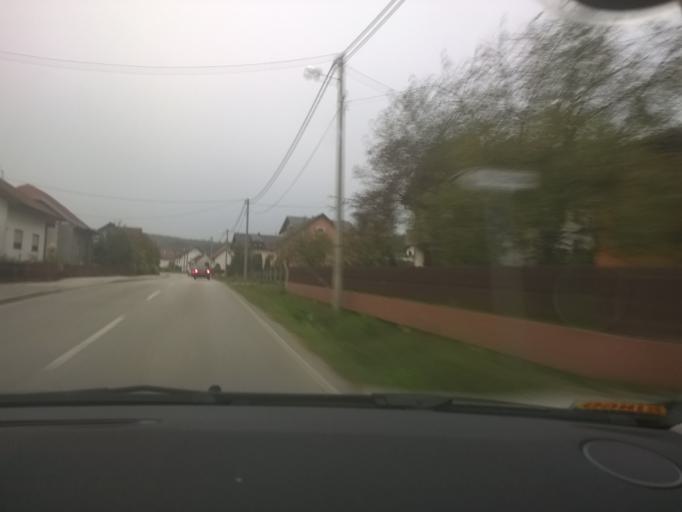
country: HR
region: Zagrebacka
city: Pojatno
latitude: 45.9017
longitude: 15.8001
